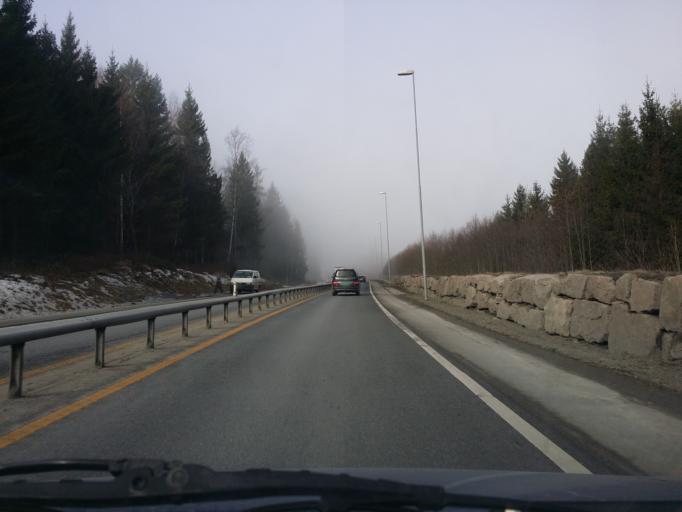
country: NO
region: Buskerud
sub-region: Drammen
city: Drammen
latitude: 59.7409
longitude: 10.1384
